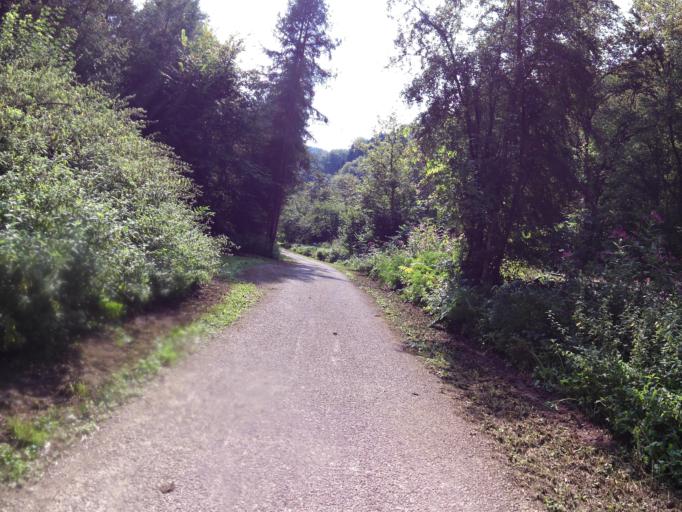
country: DE
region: Rheinland-Pfalz
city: Hosten
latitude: 49.8806
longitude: 6.6018
